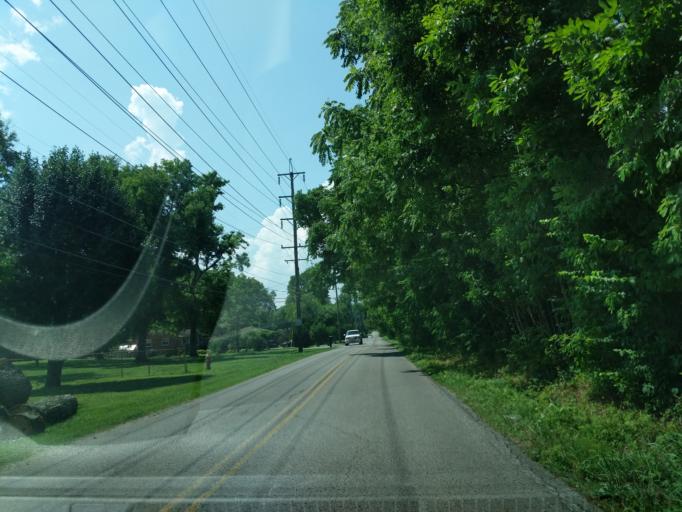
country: US
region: Tennessee
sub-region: Davidson County
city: Lakewood
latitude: 36.2796
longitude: -86.6725
